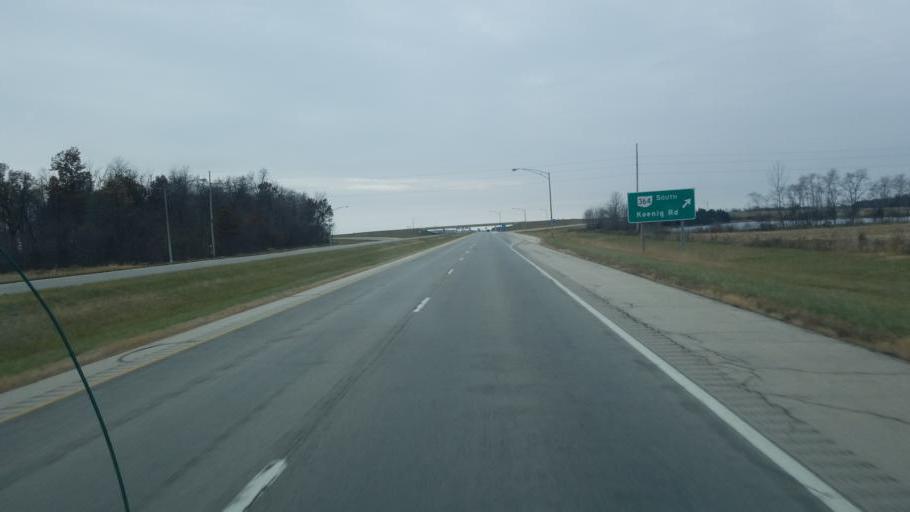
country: US
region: Ohio
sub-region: Auglaize County
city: Saint Marys
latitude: 40.5574
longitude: -84.4378
